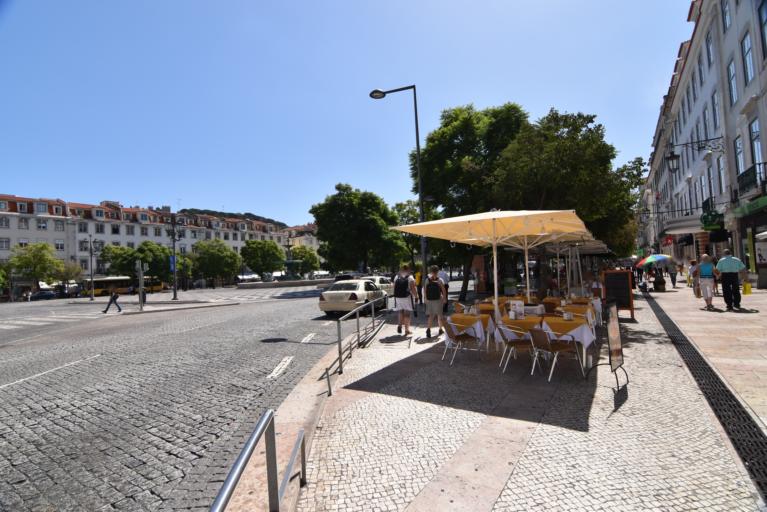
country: PT
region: Lisbon
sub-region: Lisbon
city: Lisbon
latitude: 38.7144
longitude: -9.1402
